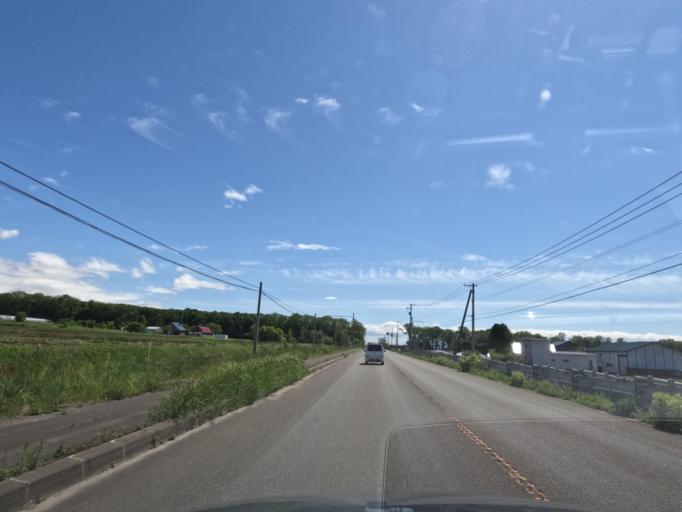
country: JP
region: Hokkaido
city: Iwamizawa
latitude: 43.0532
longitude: 141.7298
